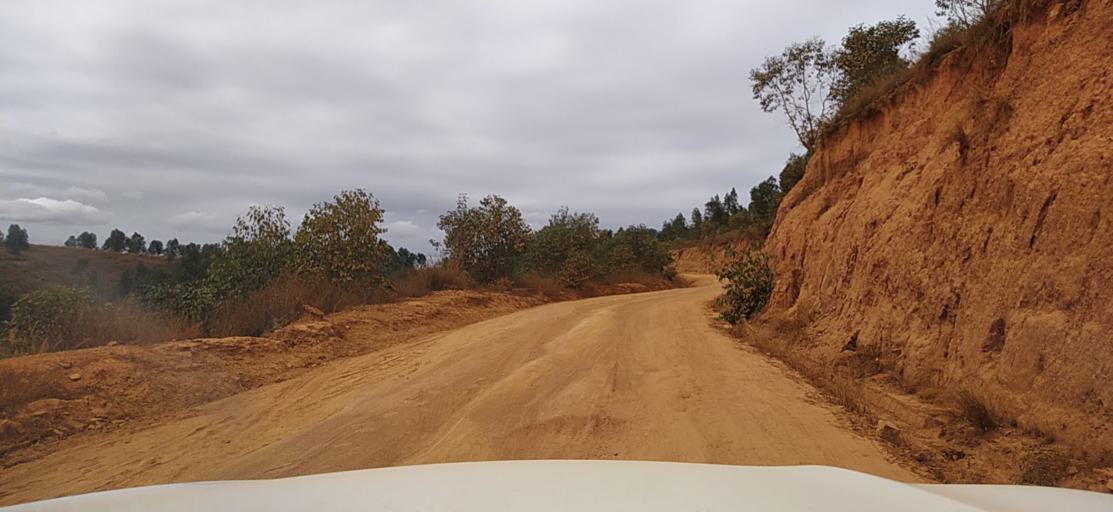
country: MG
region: Alaotra Mangoro
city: Ambatondrazaka
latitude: -17.9980
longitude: 48.2659
